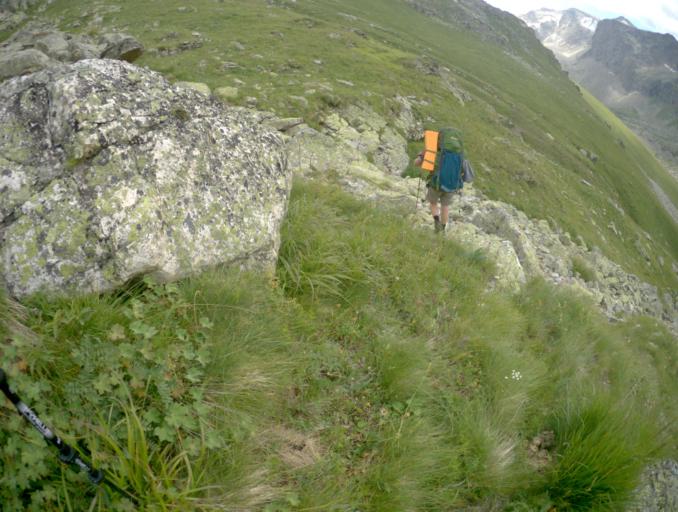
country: RU
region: Karachayevo-Cherkesiya
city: Uchkulan
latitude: 43.2947
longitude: 42.0775
